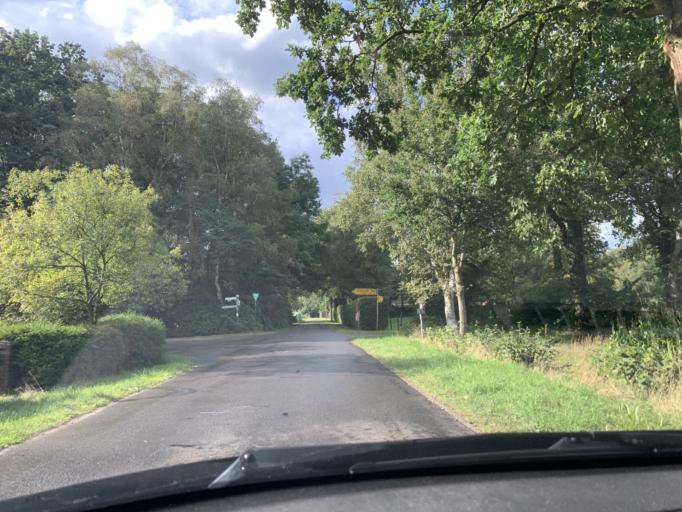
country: DE
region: Lower Saxony
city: Bockhorn
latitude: 53.3184
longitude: 7.9974
